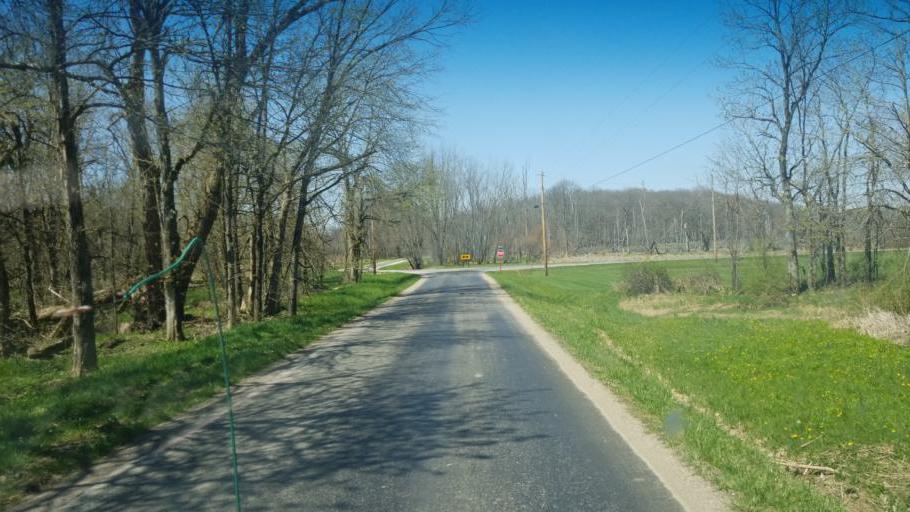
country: US
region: Ohio
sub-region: Richland County
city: Lincoln Heights
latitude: 40.8734
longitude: -82.4545
